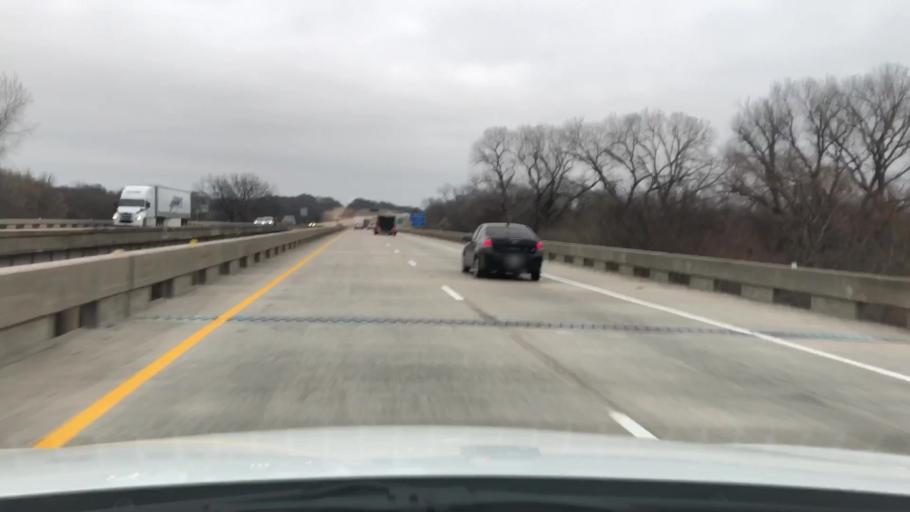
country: US
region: Texas
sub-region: Cooke County
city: Gainesville
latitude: 33.7279
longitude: -97.1591
